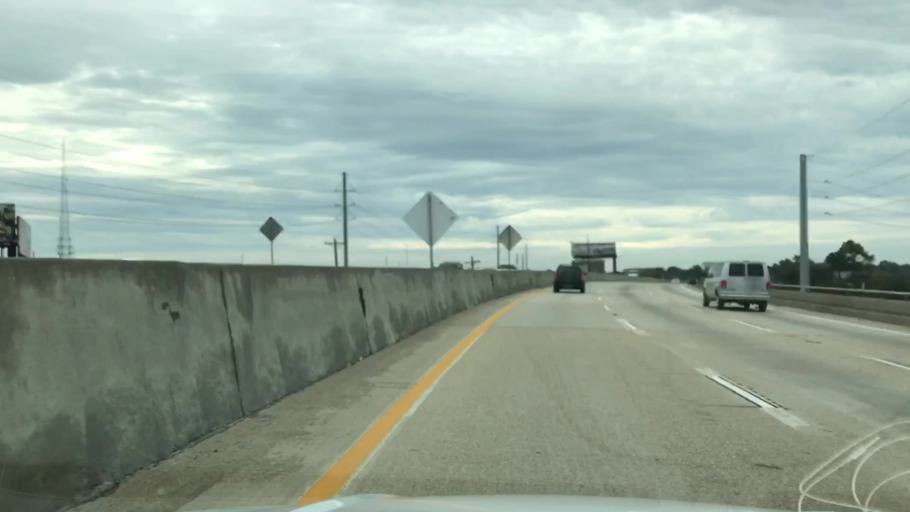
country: US
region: South Carolina
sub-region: Charleston County
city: North Charleston
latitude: 32.8251
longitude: -79.9533
